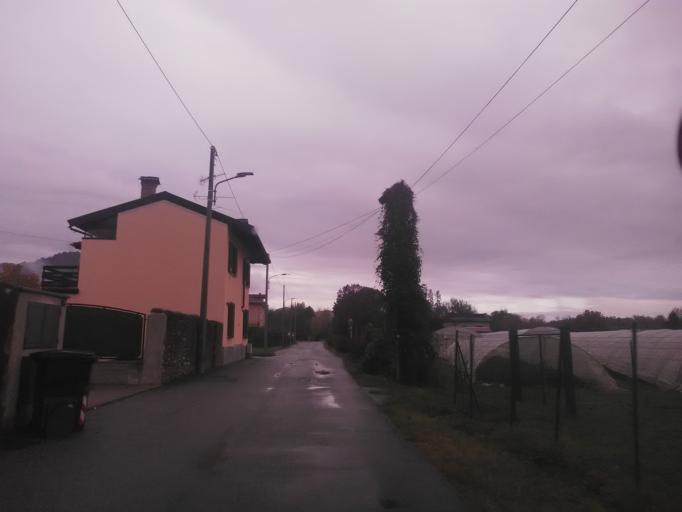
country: IT
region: Piedmont
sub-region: Provincia di Vercelli
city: Gattinara
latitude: 45.6172
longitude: 8.3748
